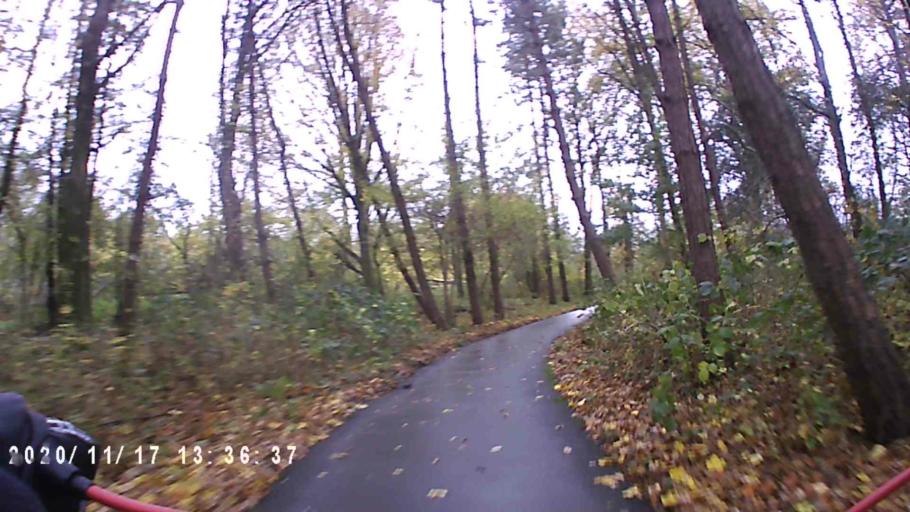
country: NL
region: Groningen
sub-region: Gemeente Zuidhorn
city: Zuidhorn
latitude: 53.2484
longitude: 6.3923
